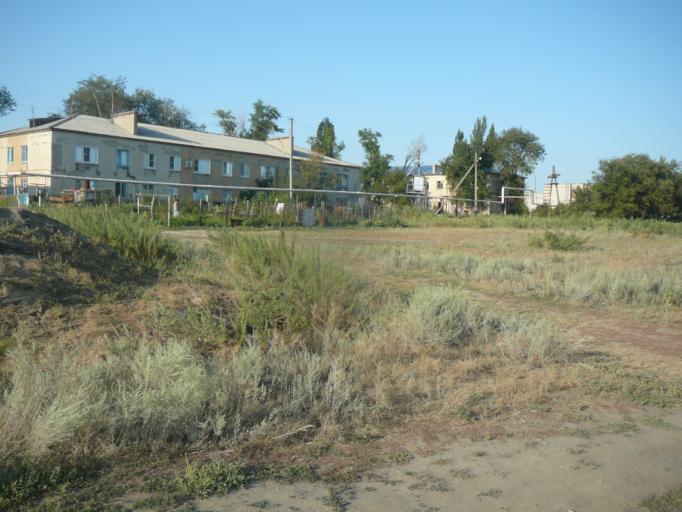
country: RU
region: Saratov
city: Sovetskoye
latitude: 51.5104
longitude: 46.6283
